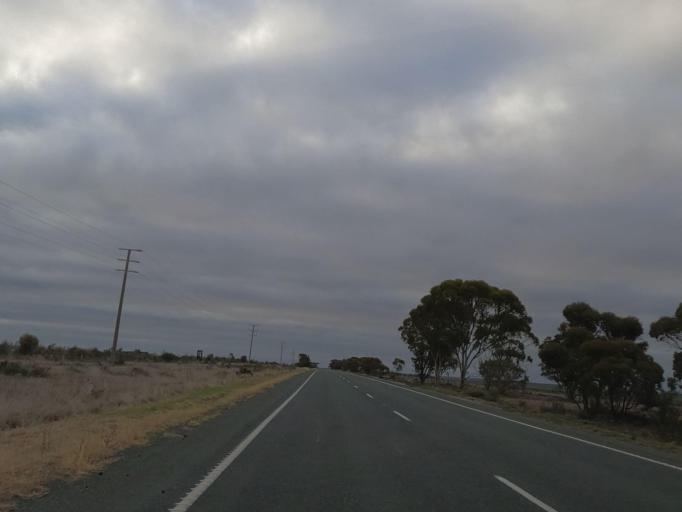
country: AU
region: Victoria
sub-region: Swan Hill
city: Swan Hill
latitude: -35.5745
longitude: 143.7874
